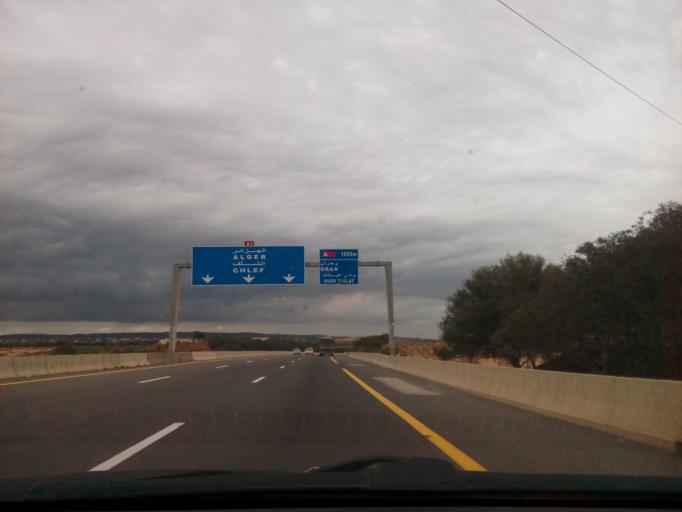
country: DZ
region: Mascara
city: Sig
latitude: 35.5337
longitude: -0.3490
